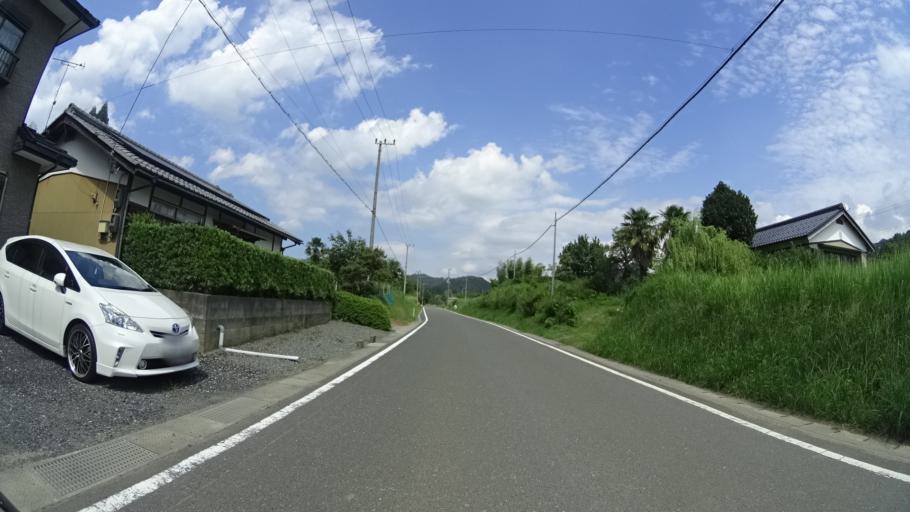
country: JP
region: Kyoto
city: Maizuru
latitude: 35.3624
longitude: 135.3192
